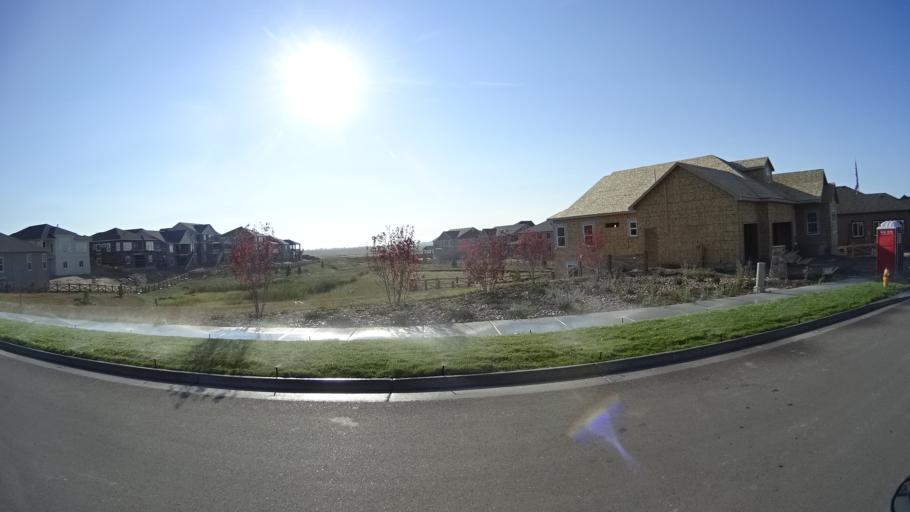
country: US
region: Colorado
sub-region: El Paso County
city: Cimarron Hills
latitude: 38.9328
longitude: -104.6545
